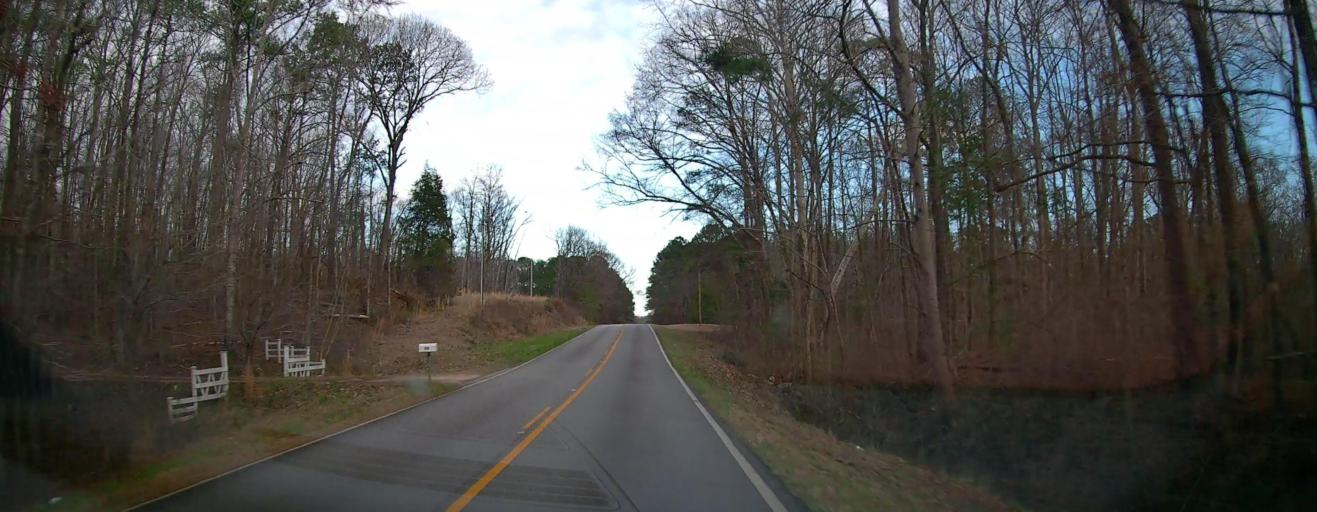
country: US
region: Georgia
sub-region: Troup County
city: West Point
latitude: 32.9438
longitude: -85.1434
